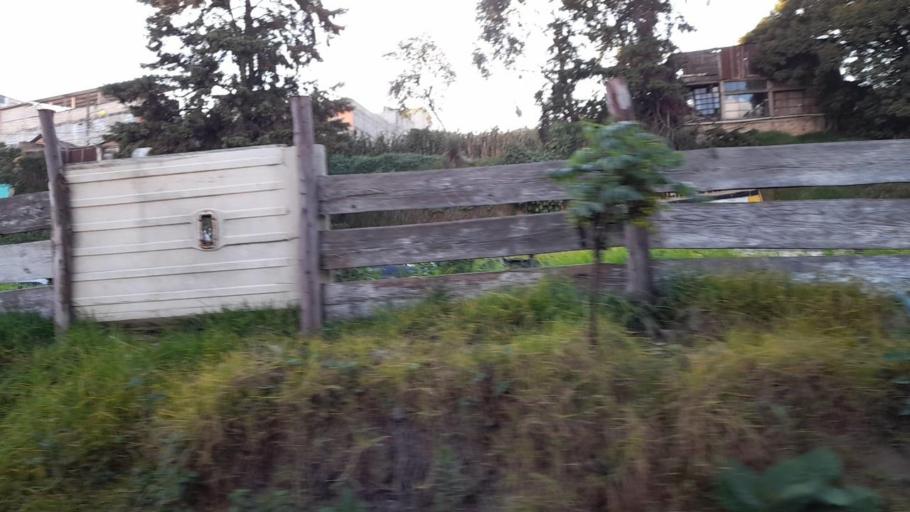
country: GT
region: Quetzaltenango
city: Quetzaltenango
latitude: 14.8374
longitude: -91.5144
